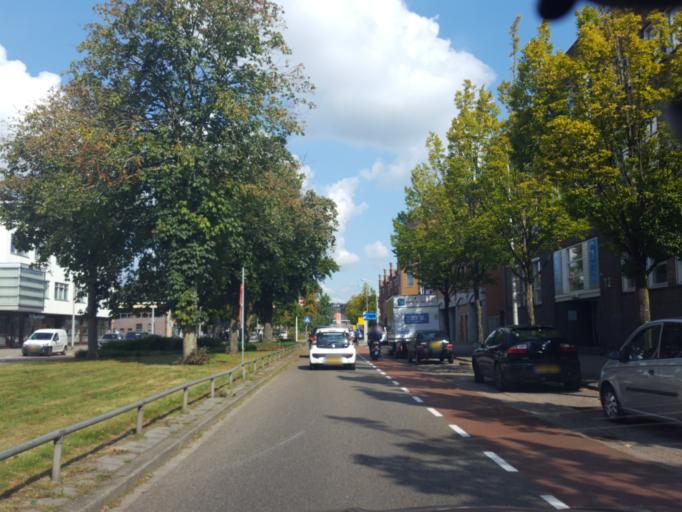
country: NL
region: Limburg
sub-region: Gemeente Weert
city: Weert
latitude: 51.2517
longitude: 5.7042
